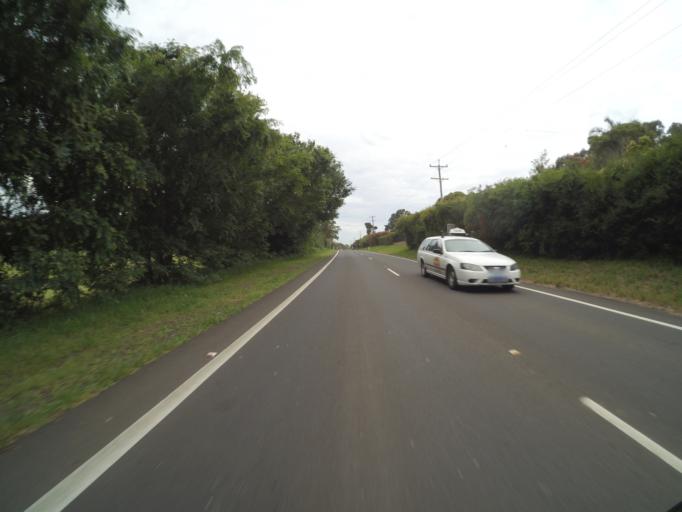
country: AU
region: New South Wales
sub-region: Kiama
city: Jamberoo
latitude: -34.6491
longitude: 150.7836
